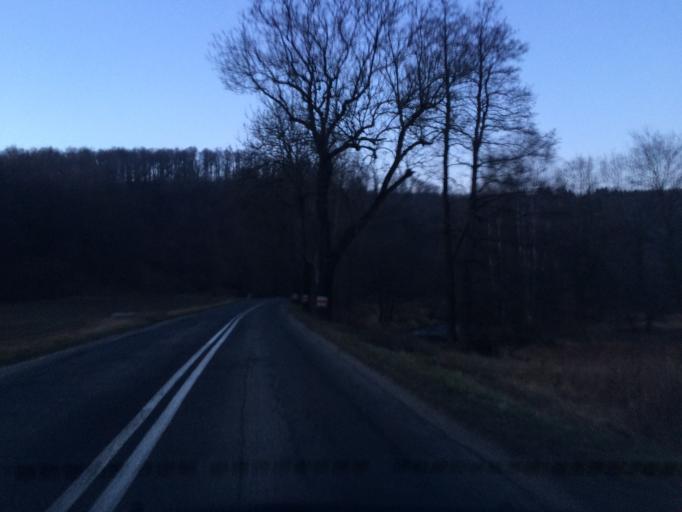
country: PL
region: Lower Silesian Voivodeship
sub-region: Powiat zlotoryjski
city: Zlotoryja
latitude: 51.1192
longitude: 15.8877
